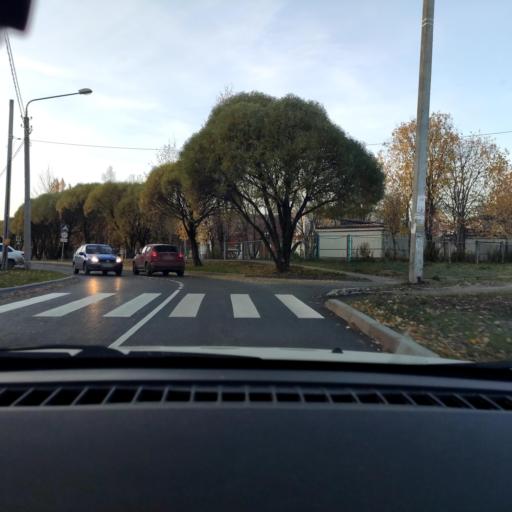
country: RU
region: Perm
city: Novyye Lyady
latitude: 58.0504
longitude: 56.5776
